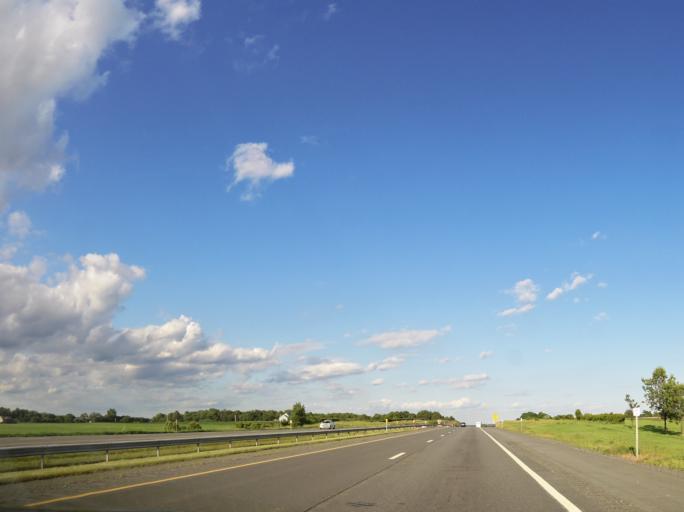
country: US
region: New York
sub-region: Genesee County
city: Batavia
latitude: 43.0218
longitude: -78.1408
